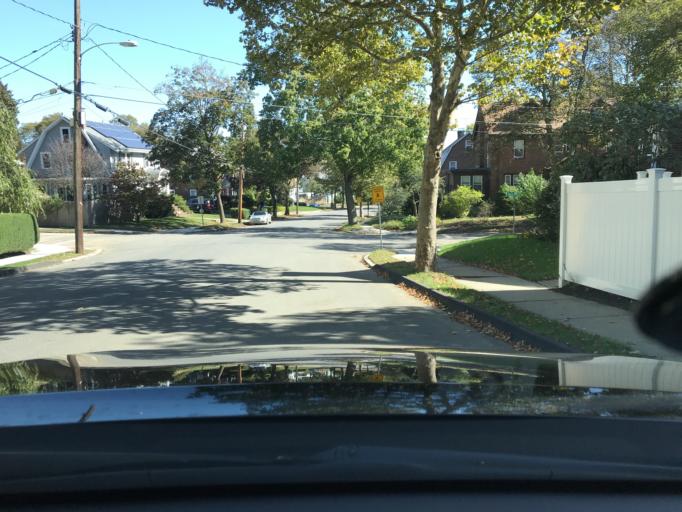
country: US
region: Massachusetts
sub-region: Middlesex County
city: Watertown
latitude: 42.3792
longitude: -71.1664
